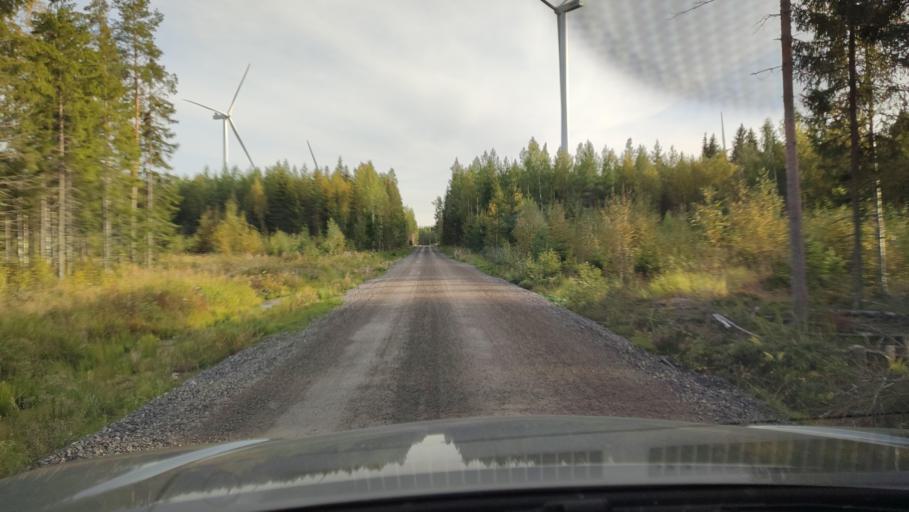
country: FI
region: Southern Ostrobothnia
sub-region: Suupohja
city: Karijoki
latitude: 62.1642
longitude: 21.6088
